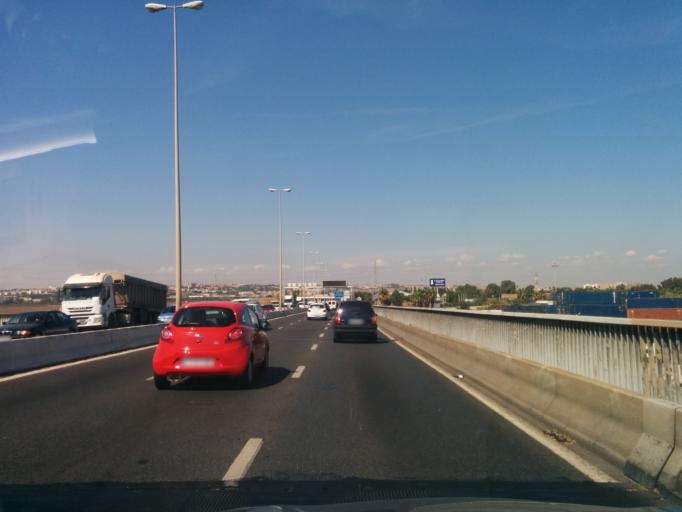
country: ES
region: Andalusia
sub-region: Provincia de Sevilla
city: Gelves
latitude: 37.3551
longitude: -6.0001
